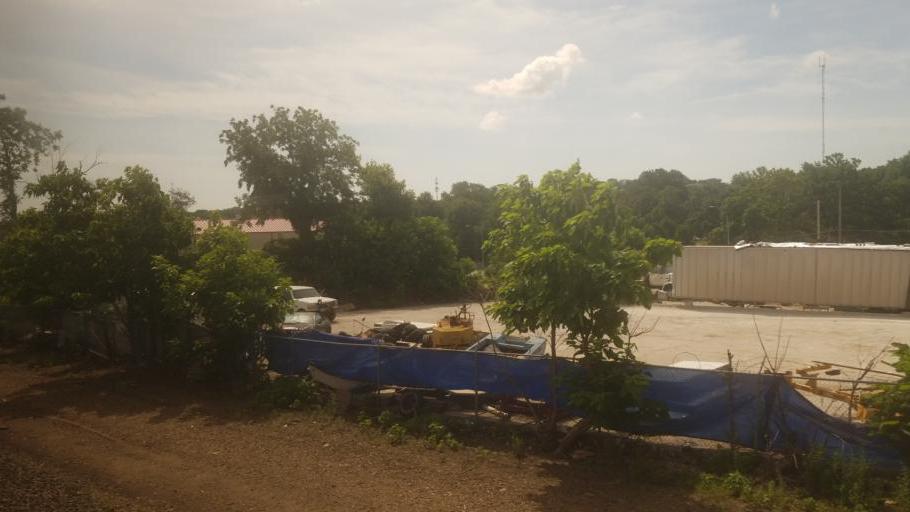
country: US
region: Missouri
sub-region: Clay County
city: North Kansas City
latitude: 39.0988
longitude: -94.5269
